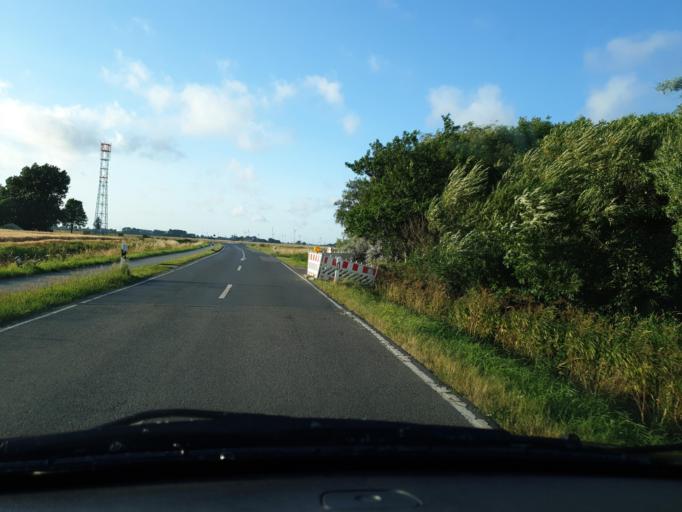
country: DE
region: Schleswig-Holstein
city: Wesselburener Deichhausen
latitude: 54.1497
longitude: 8.9175
